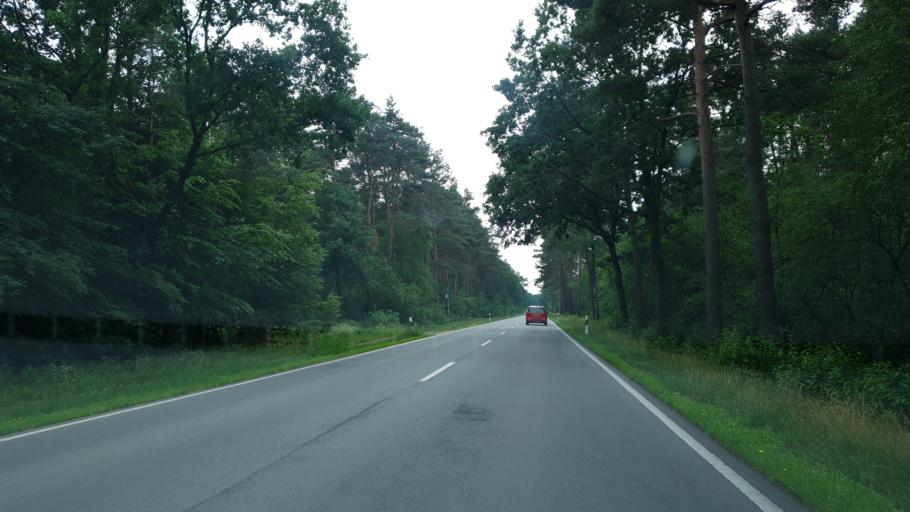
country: DE
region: Lower Saxony
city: Wietmarschen
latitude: 52.5620
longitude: 7.2019
